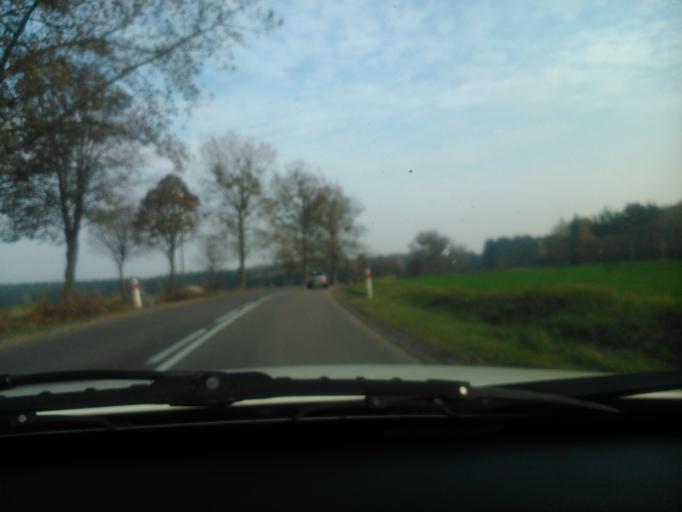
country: PL
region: Warmian-Masurian Voivodeship
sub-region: Powiat dzialdowski
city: Lidzbark
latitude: 53.2711
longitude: 19.7917
